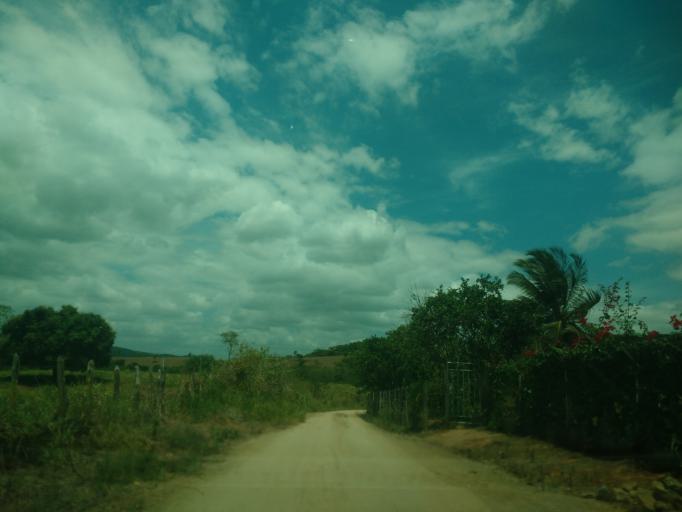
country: BR
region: Alagoas
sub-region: Santana Do Mundau
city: Santana do Mundau
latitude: -9.1571
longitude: -36.1648
